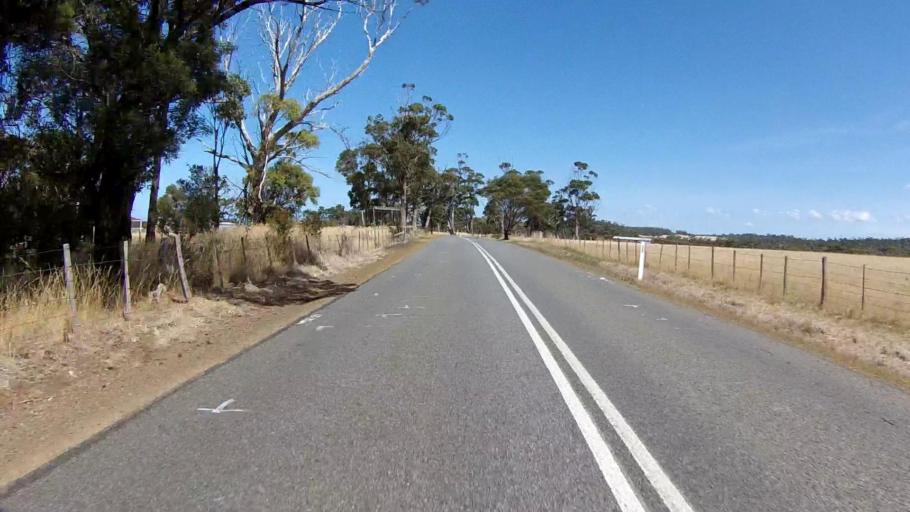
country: AU
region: Tasmania
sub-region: Sorell
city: Sorell
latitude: -42.2539
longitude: 148.0059
